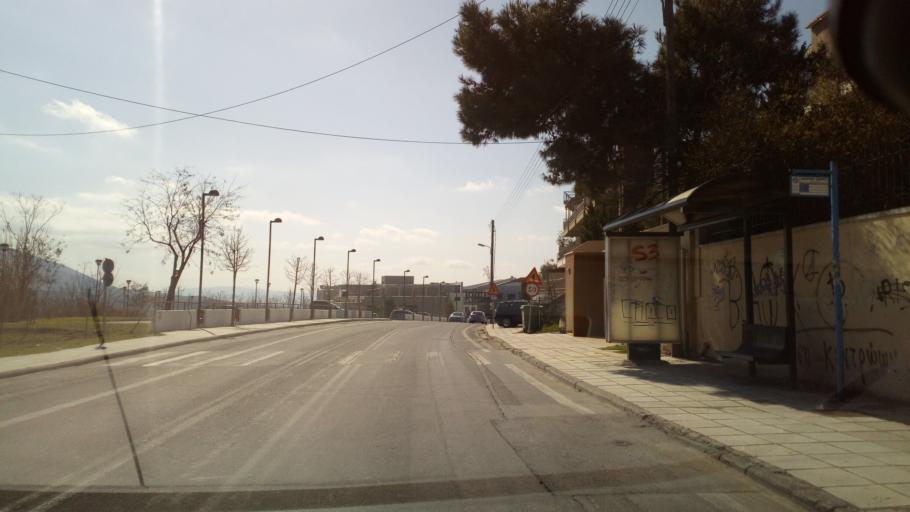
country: GR
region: Central Macedonia
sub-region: Nomos Thessalonikis
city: Panorama
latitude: 40.5871
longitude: 23.0354
